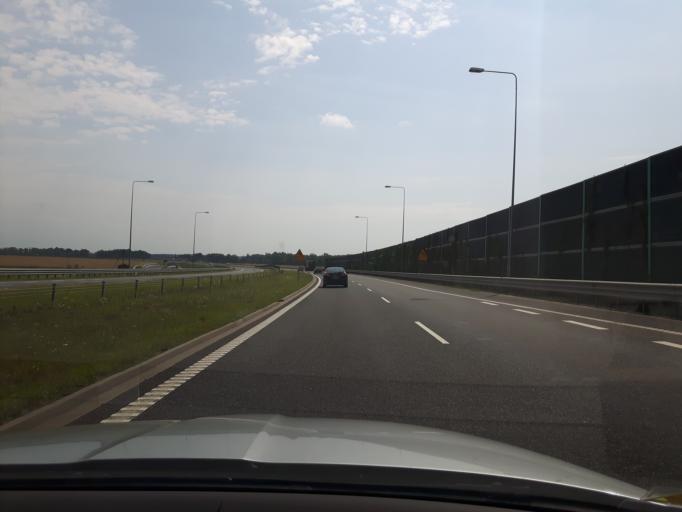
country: PL
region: Warmian-Masurian Voivodeship
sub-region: Powiat nidzicki
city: Nidzica
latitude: 53.4080
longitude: 20.3394
